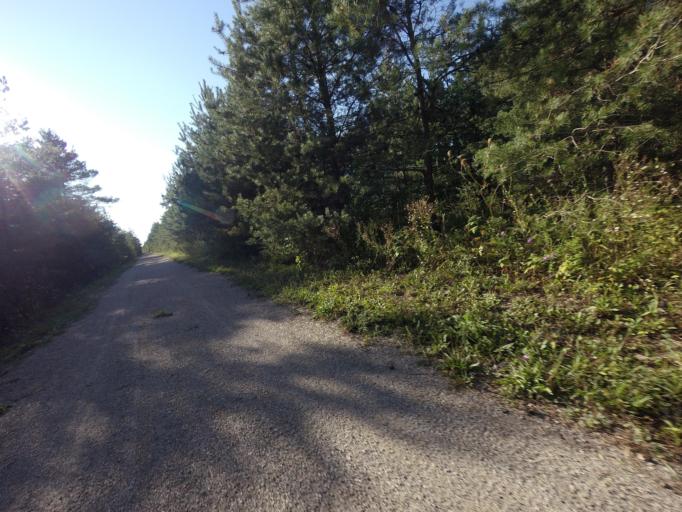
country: CA
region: Ontario
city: Goderich
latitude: 43.7529
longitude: -81.5972
